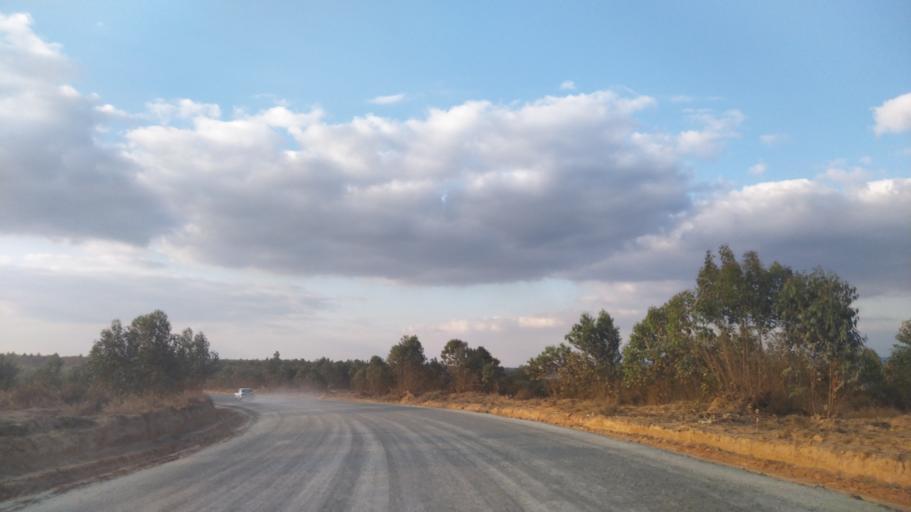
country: MG
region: Analamanga
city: Anjozorobe
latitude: -18.4869
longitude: 48.2653
